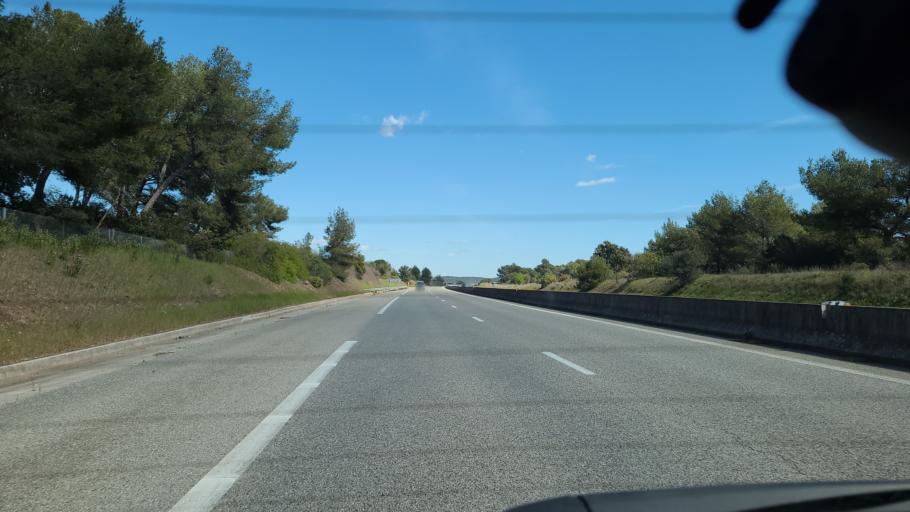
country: FR
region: Provence-Alpes-Cote d'Azur
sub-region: Departement du Var
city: Puget-Ville
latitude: 43.2600
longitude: 6.1283
